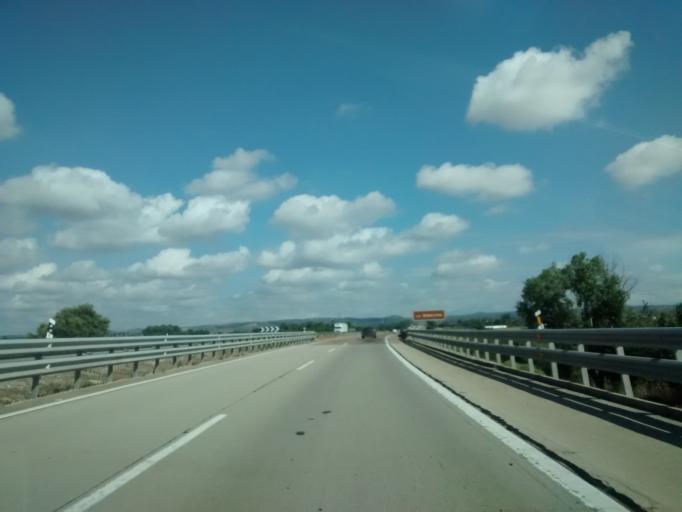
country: ES
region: Castille-La Mancha
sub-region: Province of Toledo
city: Talavera de la Reina
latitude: 39.9852
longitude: -4.7552
